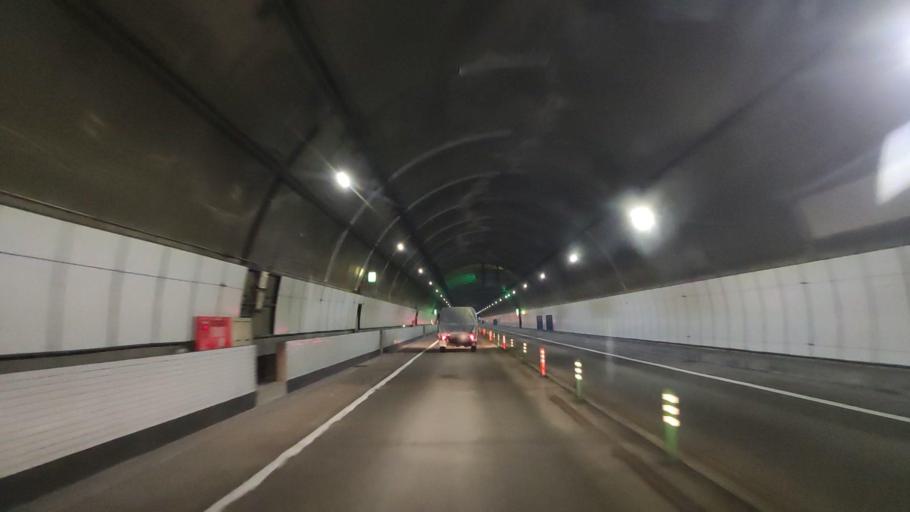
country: JP
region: Nagano
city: Hotaka
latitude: 36.1990
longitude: 137.5937
